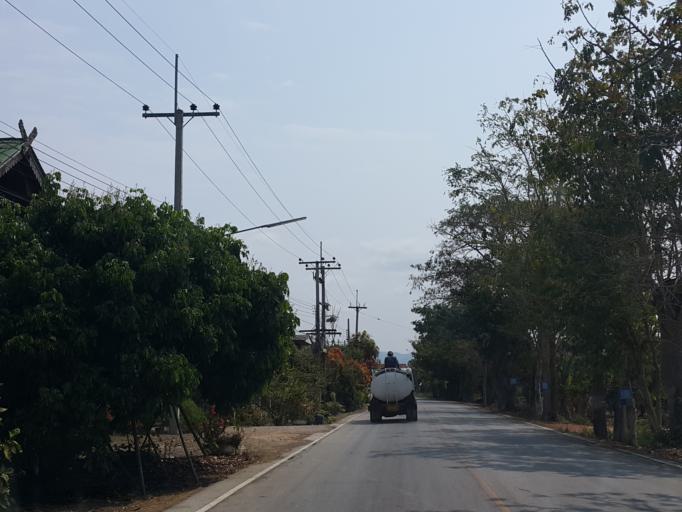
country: TH
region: Lamphun
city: Ban Thi
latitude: 18.6571
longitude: 99.1140
